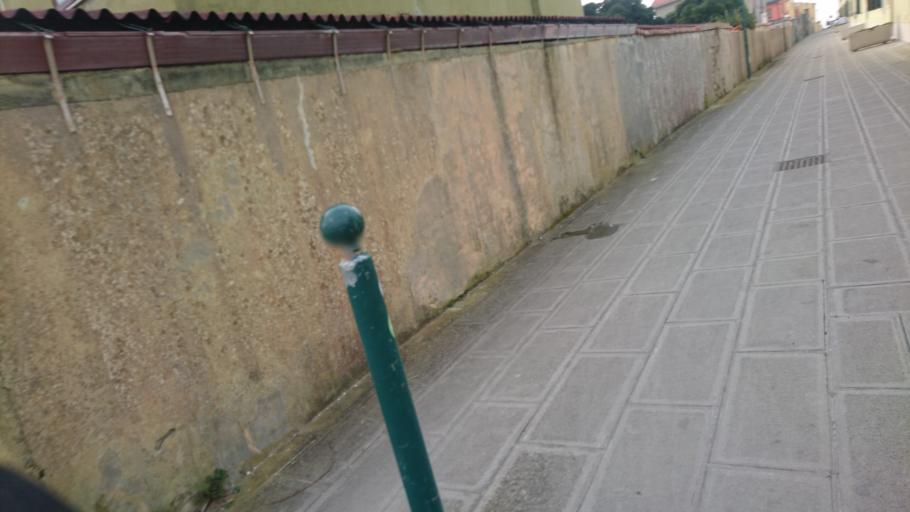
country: IT
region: Veneto
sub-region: Provincia di Venezia
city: Pellestrina
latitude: 45.2860
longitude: 12.3052
